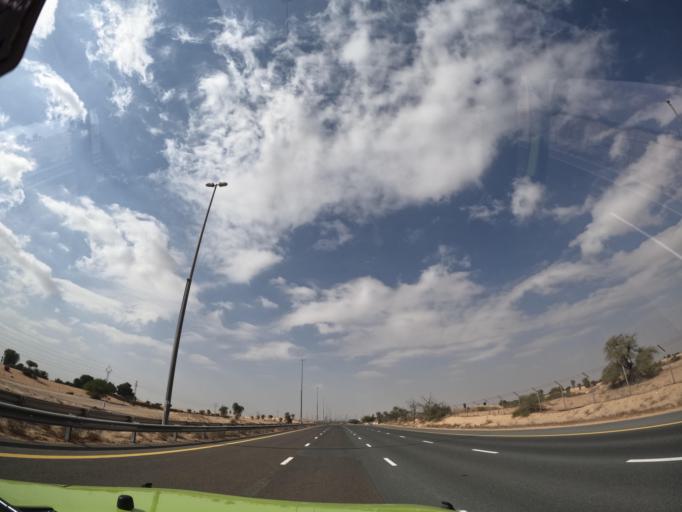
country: AE
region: Ash Shariqah
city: Sharjah
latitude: 25.0319
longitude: 55.5729
